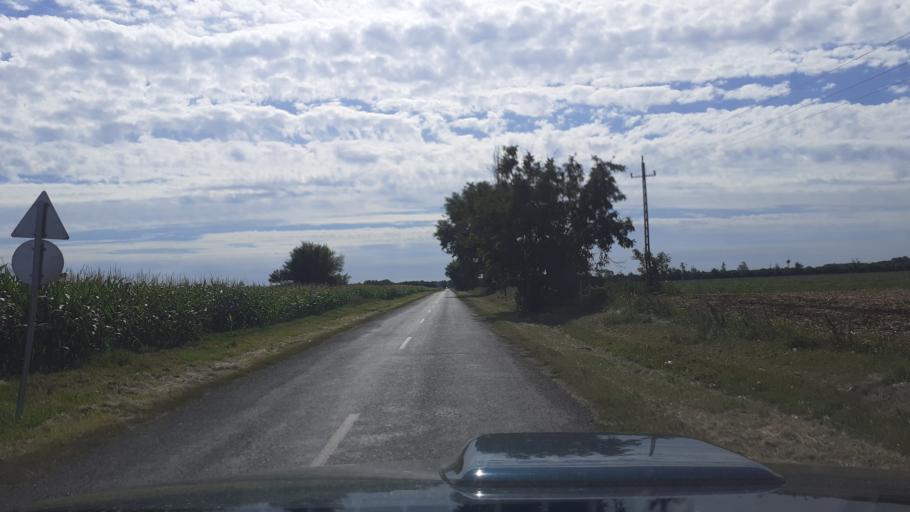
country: HU
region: Fejer
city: Pusztaszabolcs
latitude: 47.1272
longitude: 18.7684
